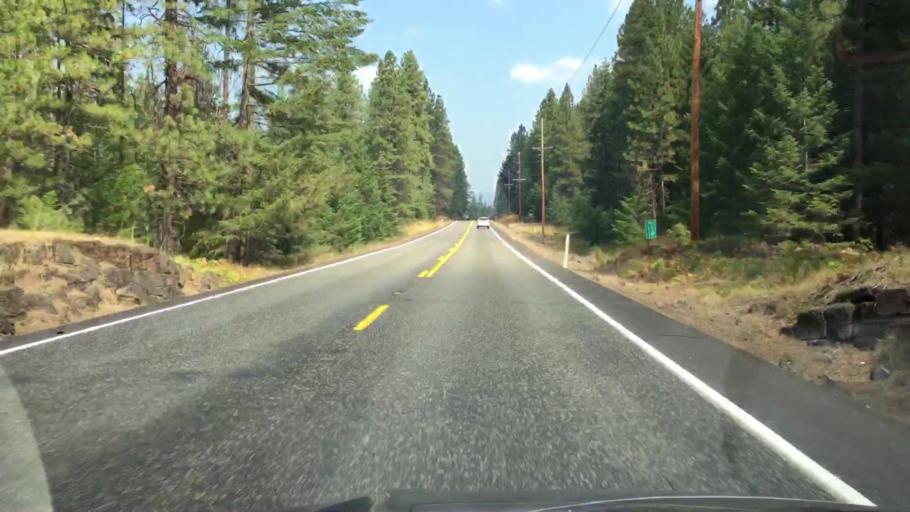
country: US
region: Washington
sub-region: Klickitat County
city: White Salmon
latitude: 45.9361
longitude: -121.4934
